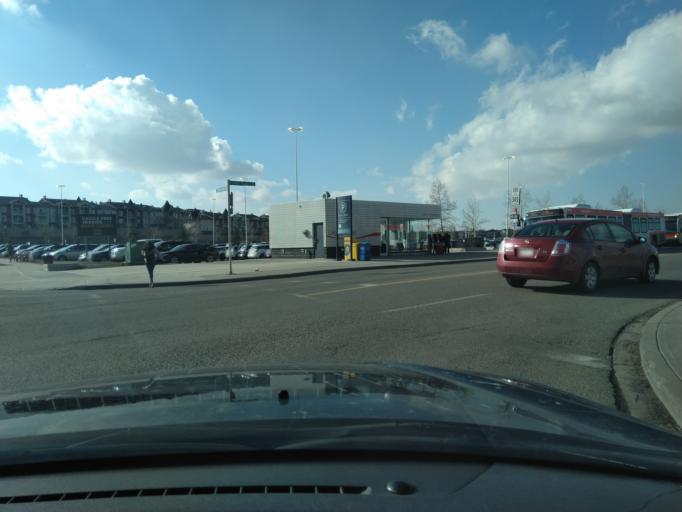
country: CA
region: Alberta
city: Calgary
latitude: 51.1568
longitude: -114.0676
